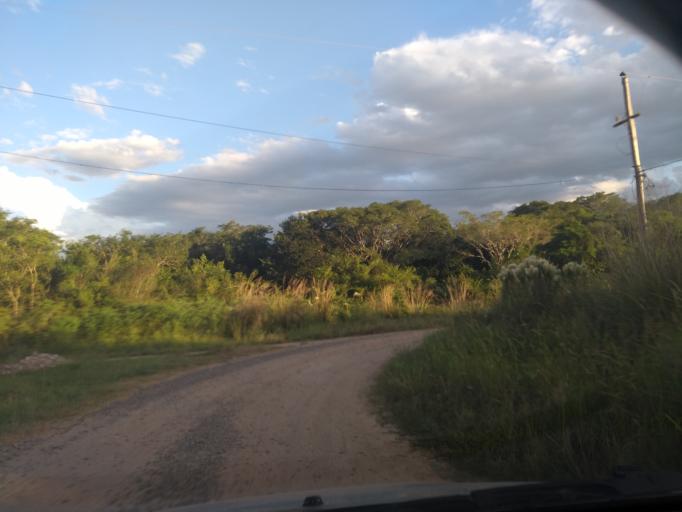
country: AR
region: Chaco
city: Colonia Benitez
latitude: -27.3942
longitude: -58.9377
